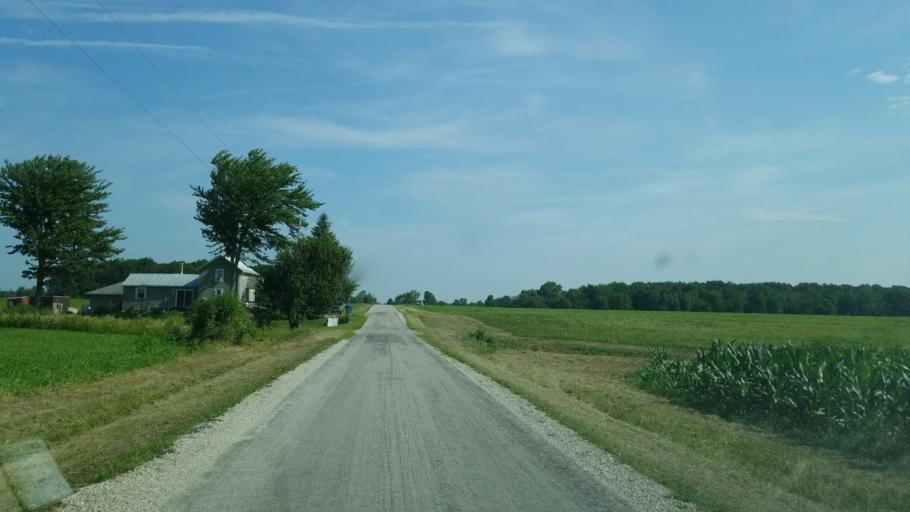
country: US
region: Ohio
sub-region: Sandusky County
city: Green Springs
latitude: 41.0990
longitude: -82.9960
